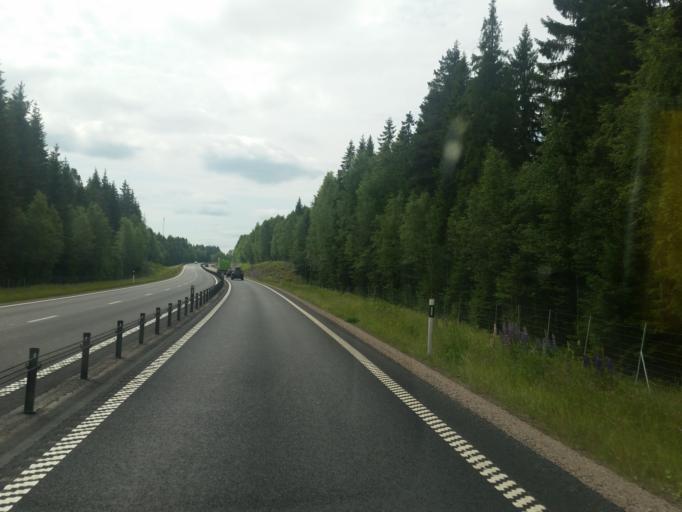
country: SE
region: Dalarna
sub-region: Borlange Kommun
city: Borlaenge
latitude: 60.4533
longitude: 15.3709
